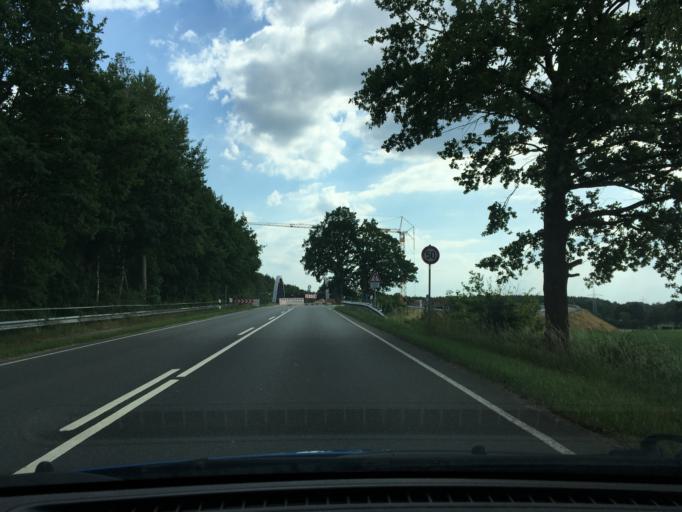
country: DE
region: Lower Saxony
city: Kakenstorf
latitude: 53.3052
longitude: 9.8006
